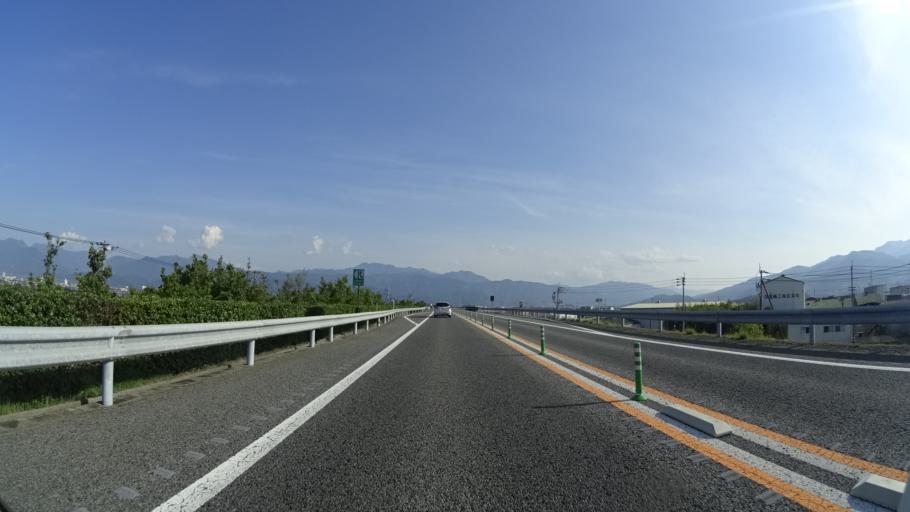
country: JP
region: Ehime
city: Saijo
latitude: 33.9412
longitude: 133.0690
